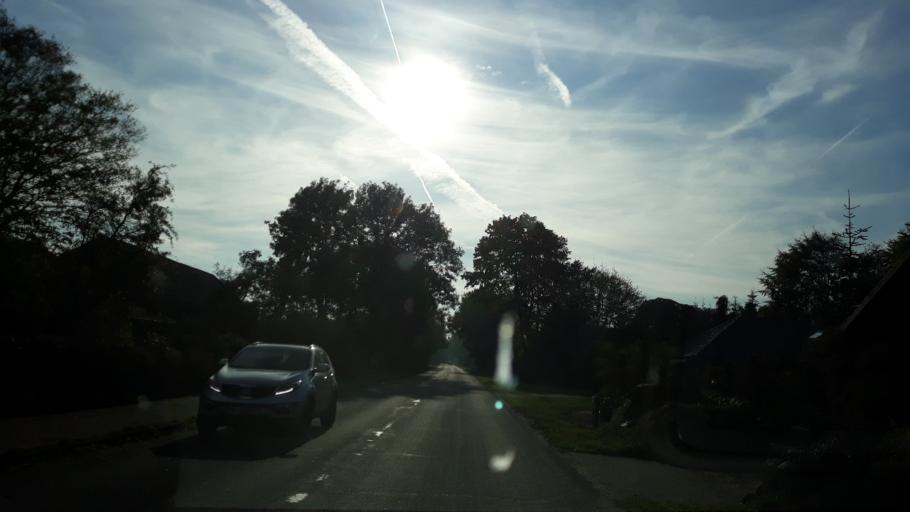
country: DE
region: Schleswig-Holstein
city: Borm
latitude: 54.4141
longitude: 9.3872
